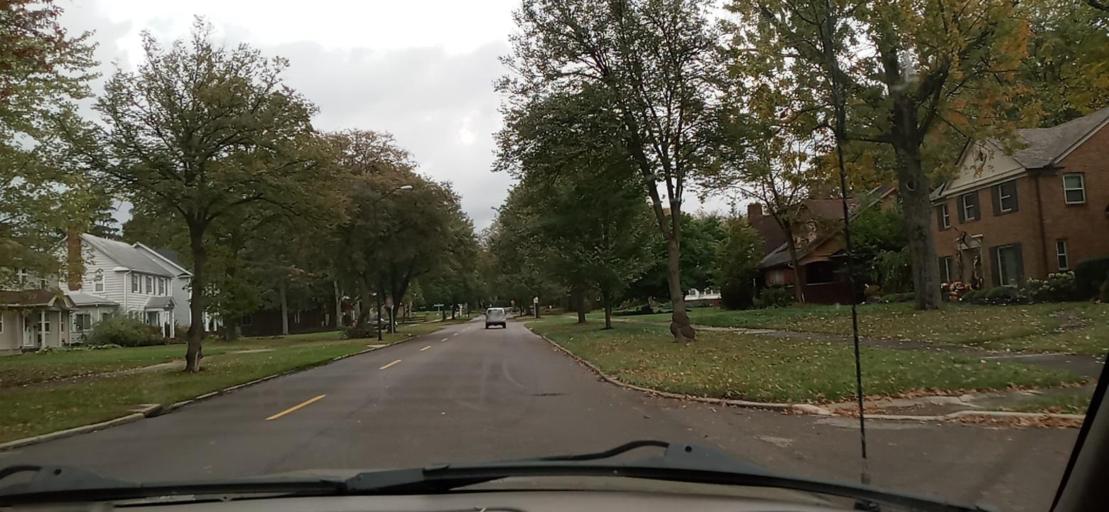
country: US
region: Ohio
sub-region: Summit County
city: Akron
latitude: 41.0924
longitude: -81.5660
